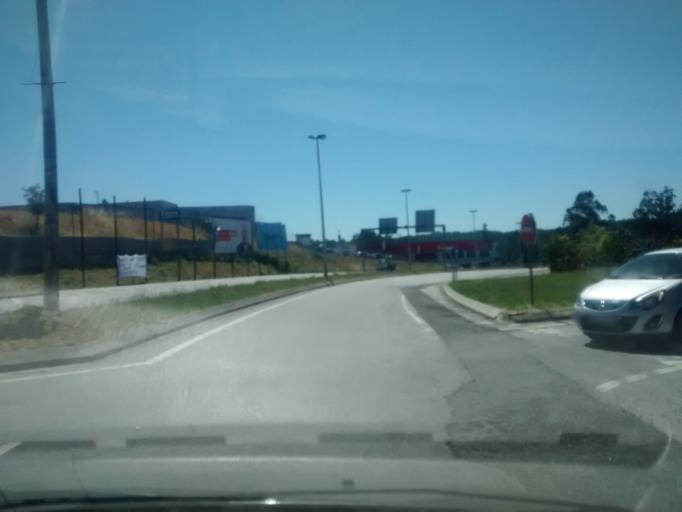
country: PT
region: Braga
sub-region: Barcelos
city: Vila Frescainha
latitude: 41.5215
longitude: -8.6308
